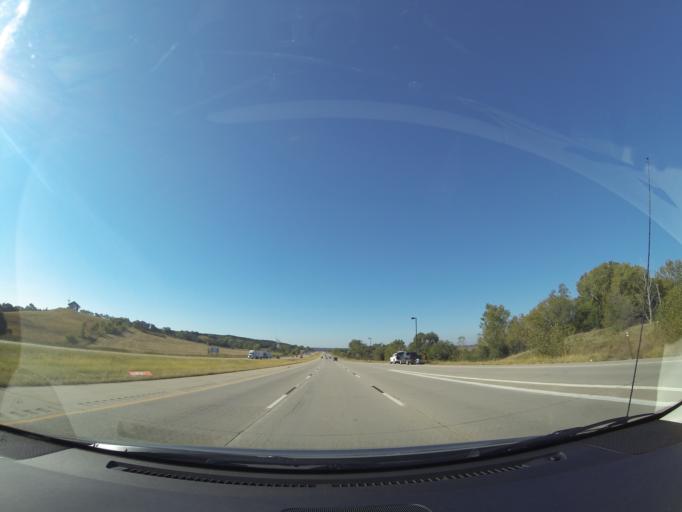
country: US
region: Nebraska
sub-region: Sarpy County
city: Gretna
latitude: 41.0792
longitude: -96.2795
